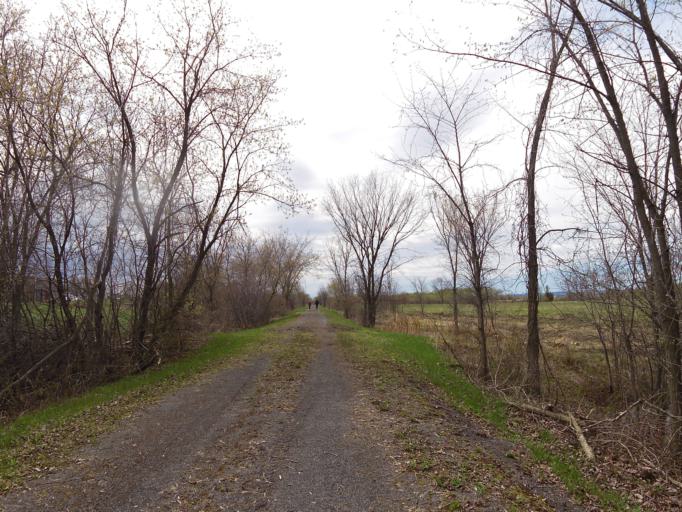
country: CA
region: Ontario
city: Hawkesbury
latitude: 45.5428
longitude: -74.7604
